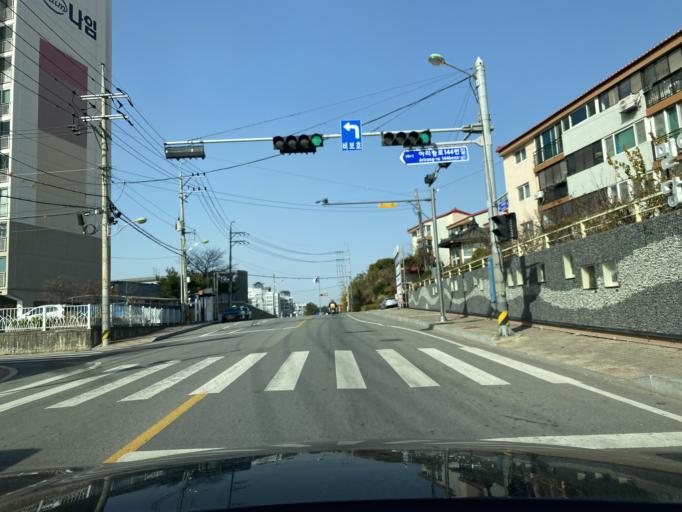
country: KR
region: Chungcheongnam-do
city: Yesan
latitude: 36.6859
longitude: 126.8451
